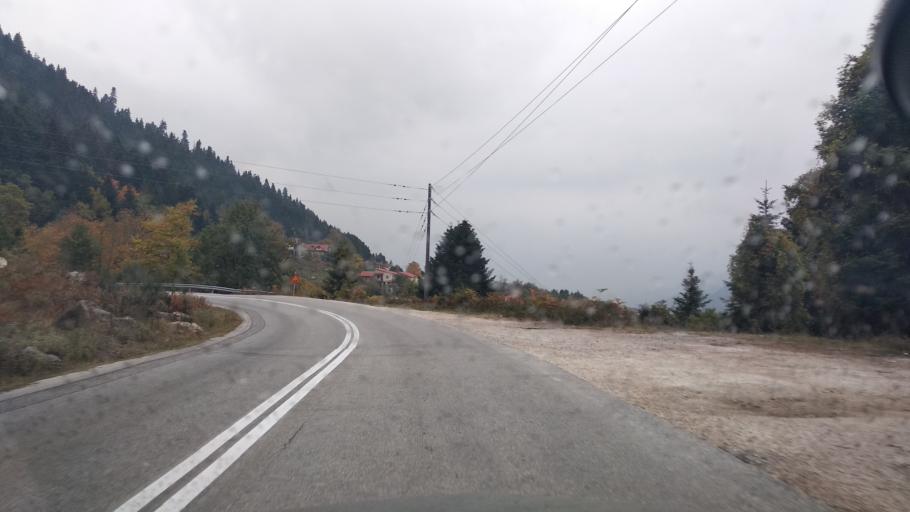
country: GR
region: Thessaly
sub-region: Trikala
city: Pyli
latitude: 39.5105
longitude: 21.5321
